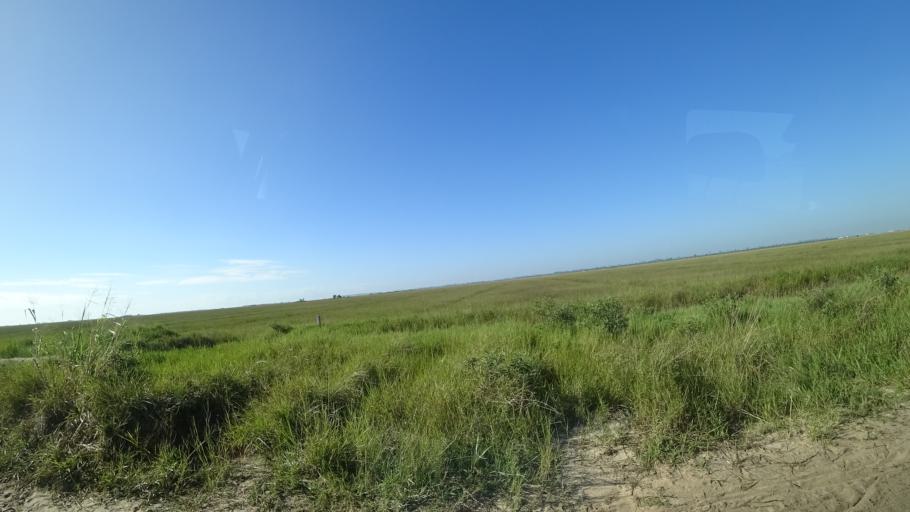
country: MZ
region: Sofala
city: Beira
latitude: -19.7577
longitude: 34.9197
